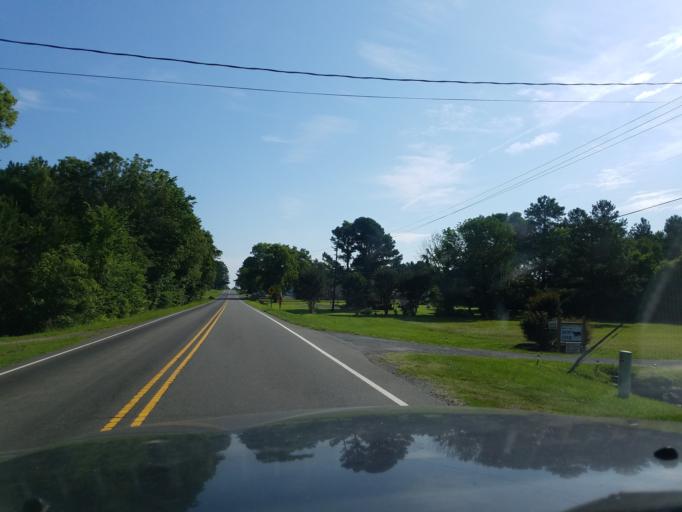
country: US
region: North Carolina
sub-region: Granville County
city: Oxford
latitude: 36.2554
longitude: -78.6599
